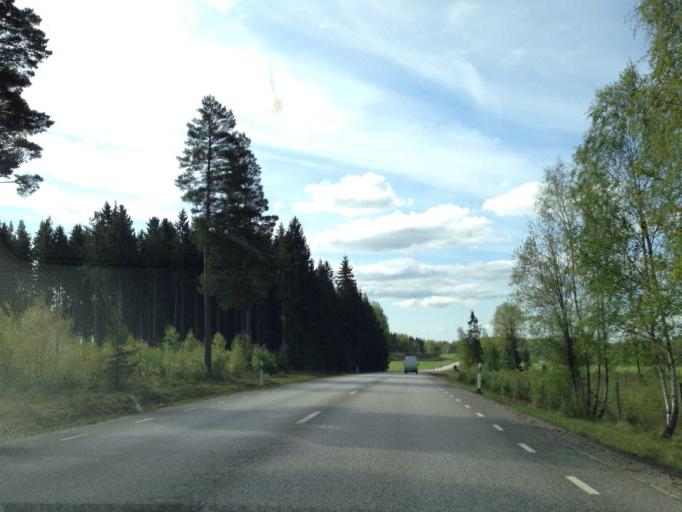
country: SE
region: Soedermanland
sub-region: Nykopings Kommun
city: Svalsta
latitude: 58.8418
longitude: 16.9223
